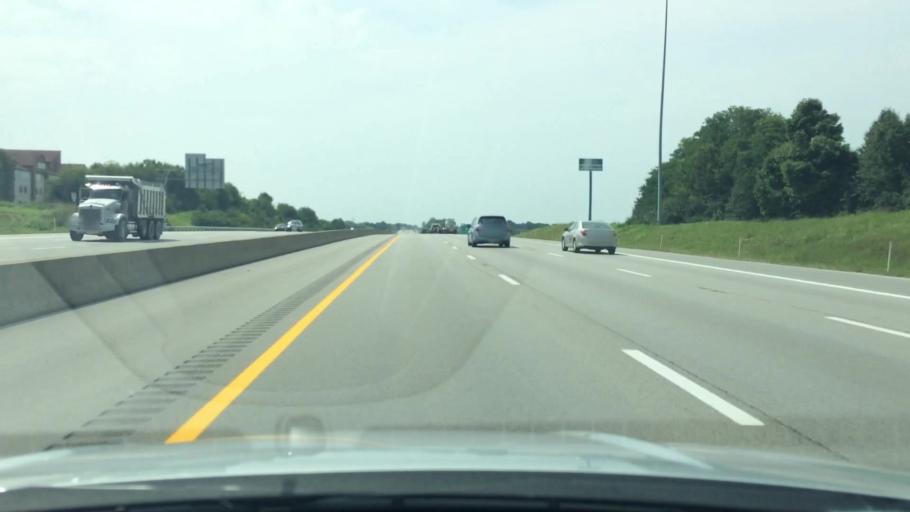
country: US
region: Kentucky
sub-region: Madison County
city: Richmond
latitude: 37.7702
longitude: -84.3168
